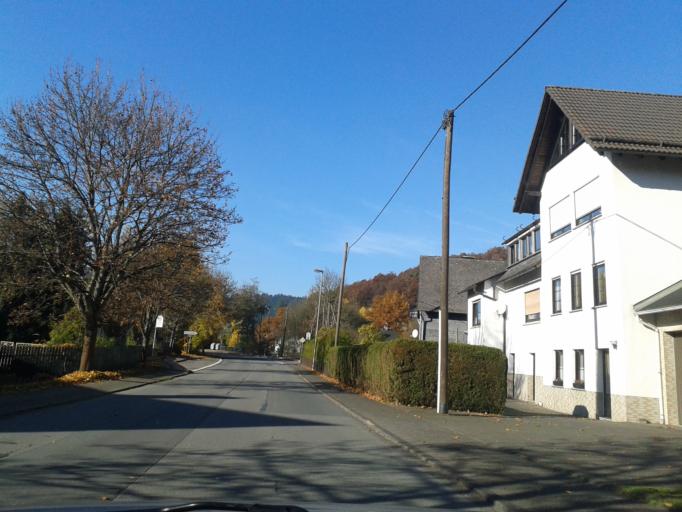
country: DE
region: North Rhine-Westphalia
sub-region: Regierungsbezirk Arnsberg
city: Bad Laasphe
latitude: 50.8732
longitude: 8.3557
